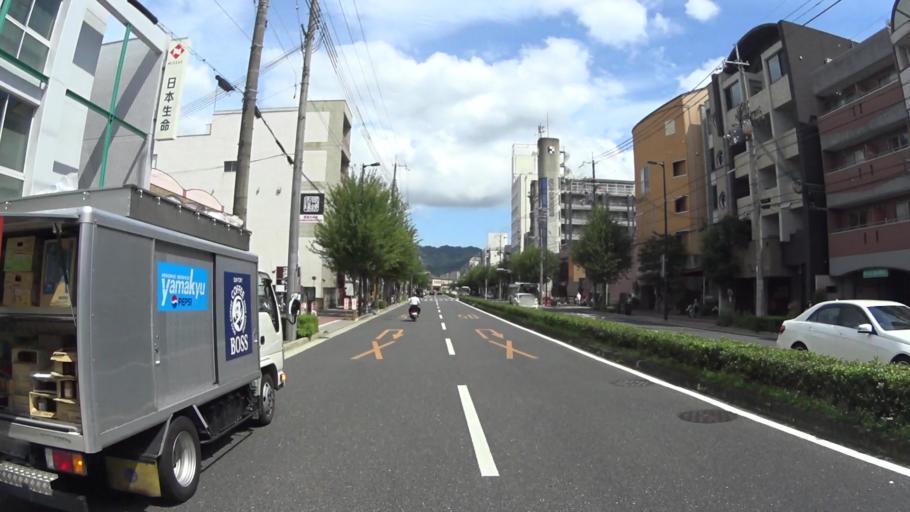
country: JP
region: Kyoto
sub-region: Kyoto-shi
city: Kamigyo-ku
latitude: 35.0441
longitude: 135.7725
